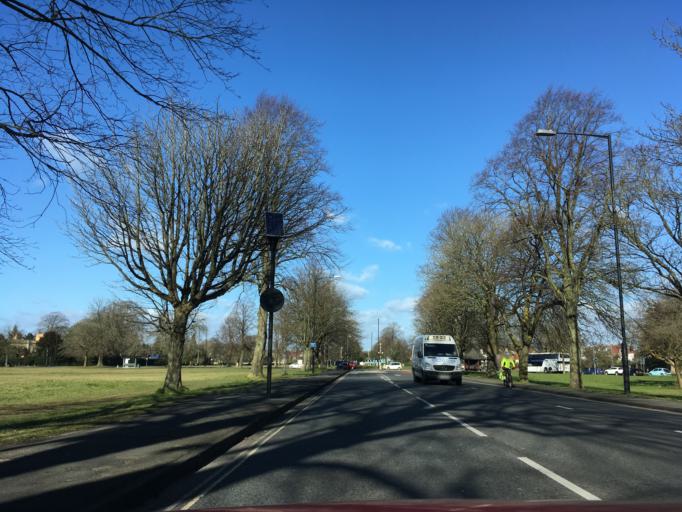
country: GB
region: England
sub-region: Bristol
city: Bristol
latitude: 51.4780
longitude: -2.6168
